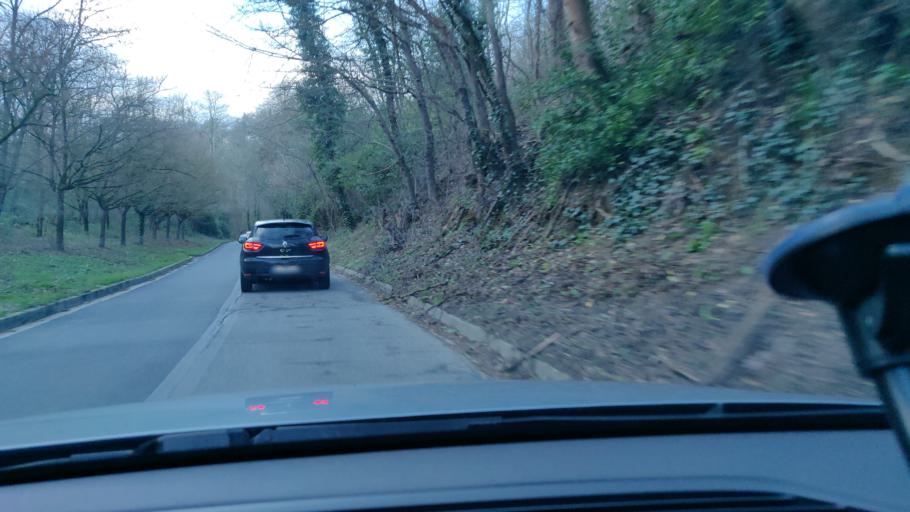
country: FR
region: Midi-Pyrenees
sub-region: Departement de la Haute-Garonne
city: Vieille-Toulouse
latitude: 43.5494
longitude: 1.4467
